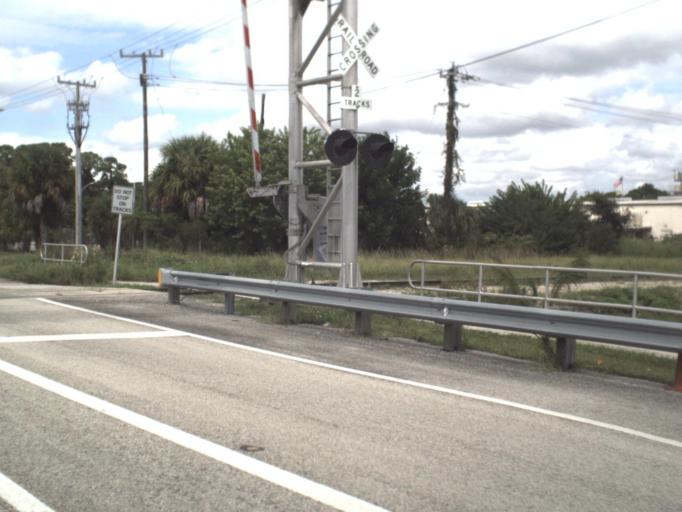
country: US
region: Florida
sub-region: Sarasota County
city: North Sarasota
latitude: 27.3888
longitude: -82.5302
